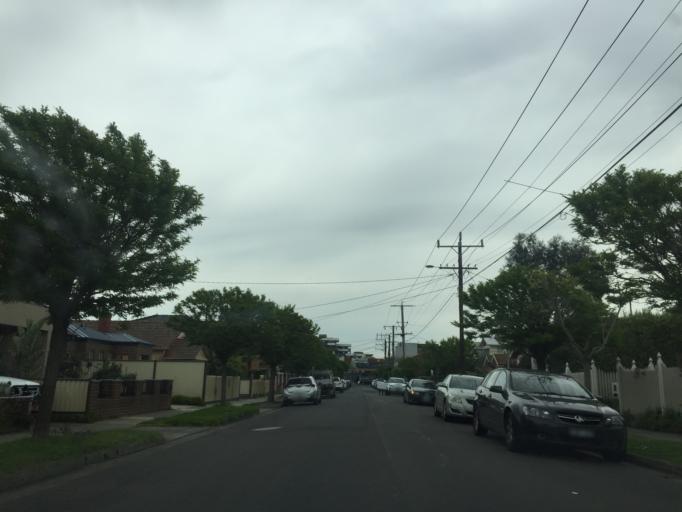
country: AU
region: Victoria
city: Thornbury
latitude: -37.7374
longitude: 145.0061
